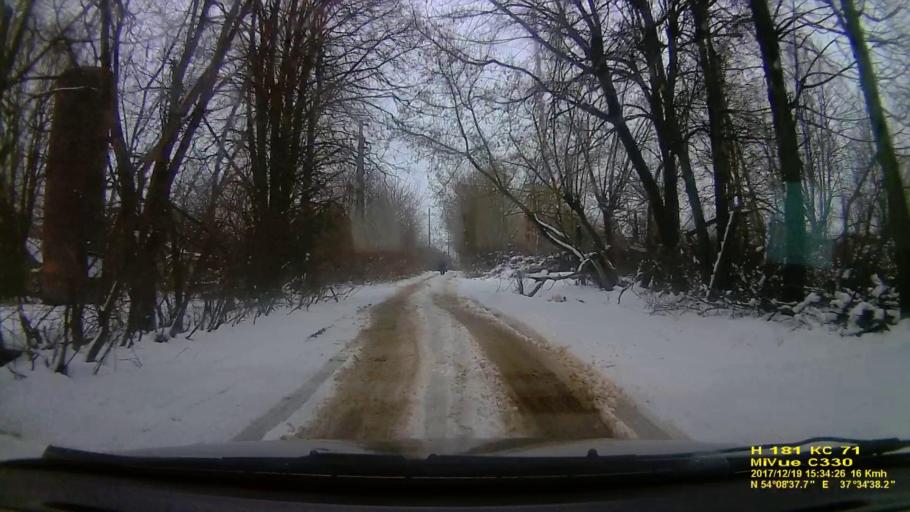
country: RU
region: Tula
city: Mendeleyevskiy
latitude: 54.1438
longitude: 37.5774
